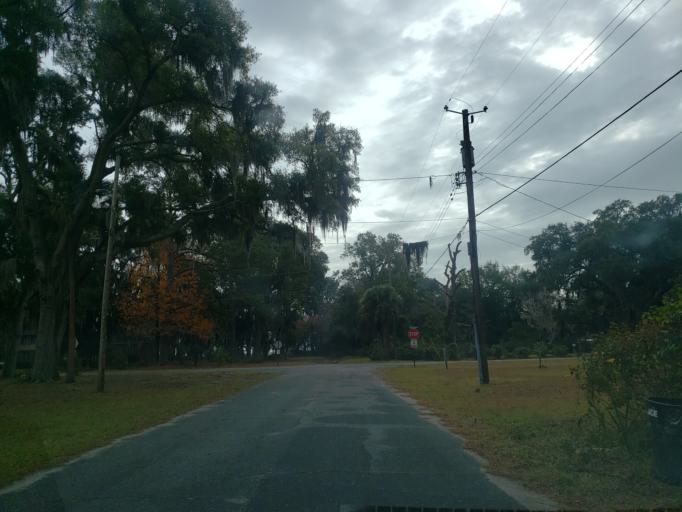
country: US
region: Georgia
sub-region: Chatham County
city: Wilmington Island
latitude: 31.9772
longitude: -80.9984
